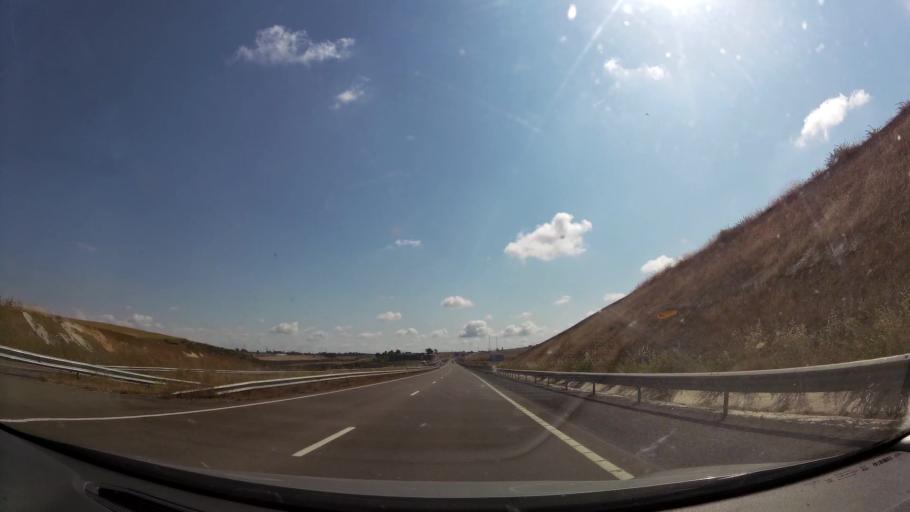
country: MA
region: Rabat-Sale-Zemmour-Zaer
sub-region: Skhirate-Temara
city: Temara
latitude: 33.8575
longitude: -6.8210
